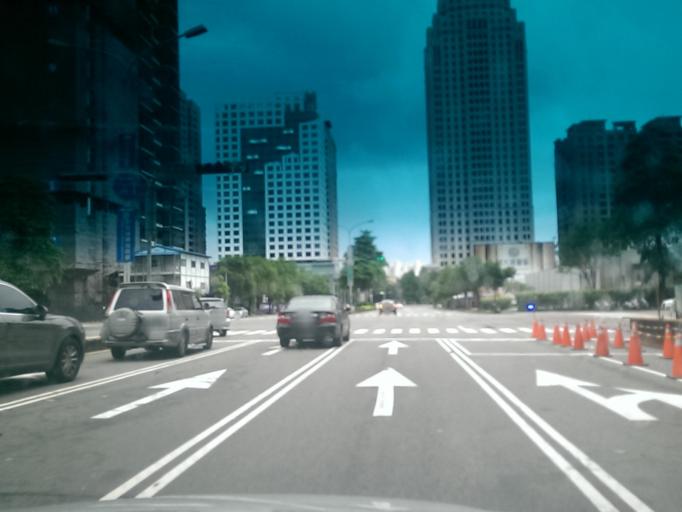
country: TW
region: Taiwan
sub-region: Taichung City
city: Taichung
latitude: 24.1590
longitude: 120.6427
